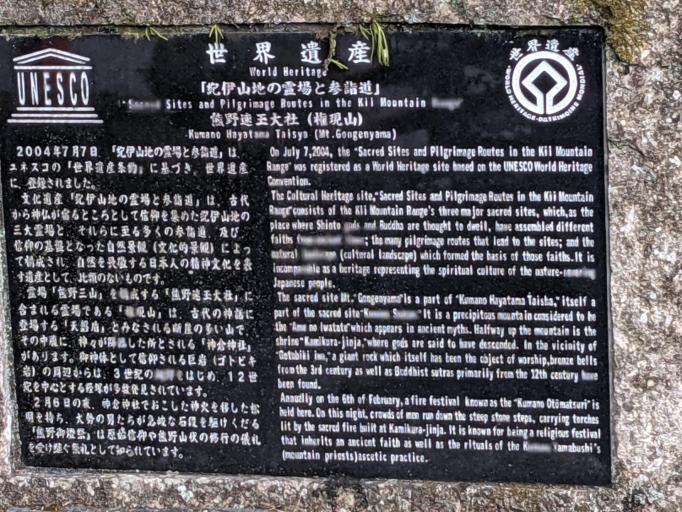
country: JP
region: Wakayama
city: Shingu
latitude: 33.7243
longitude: 135.9841
